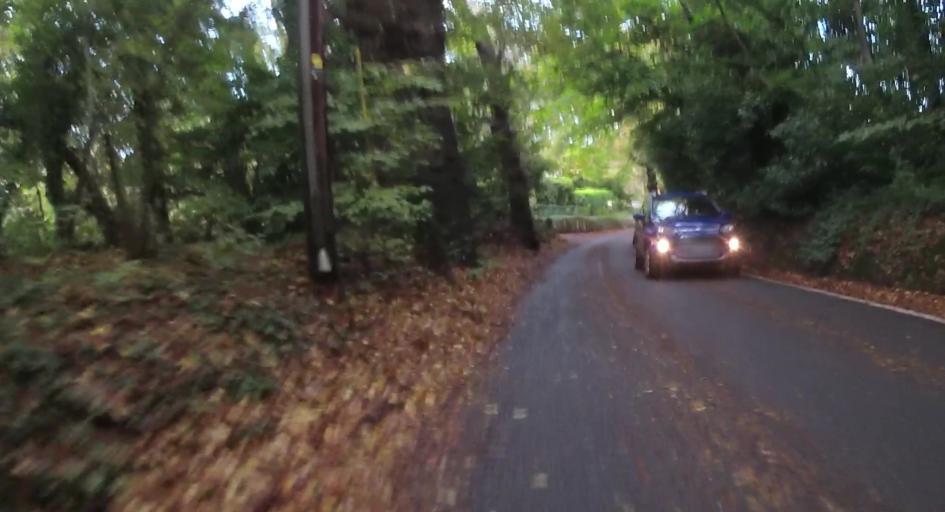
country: GB
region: England
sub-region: Hampshire
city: Four Marks
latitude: 51.1366
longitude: -1.0320
